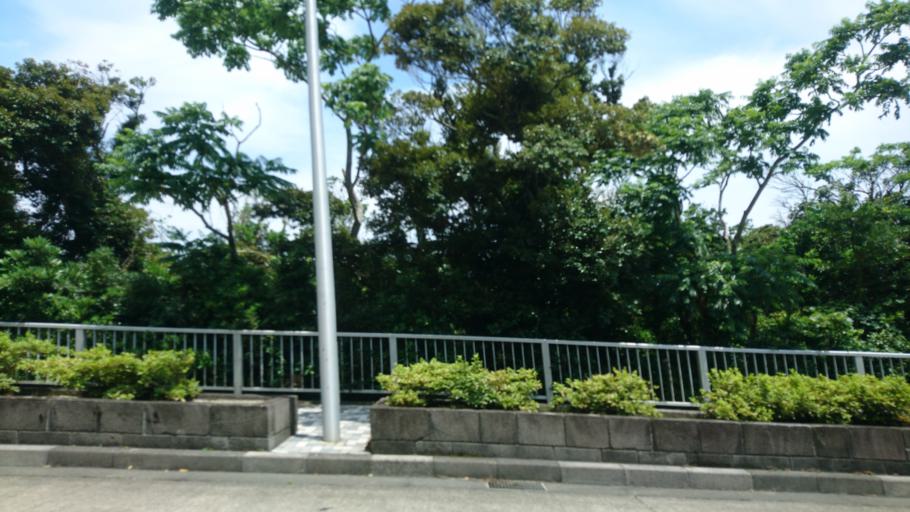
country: JP
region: Shizuoka
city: Shimoda
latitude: 34.3847
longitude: 139.2737
